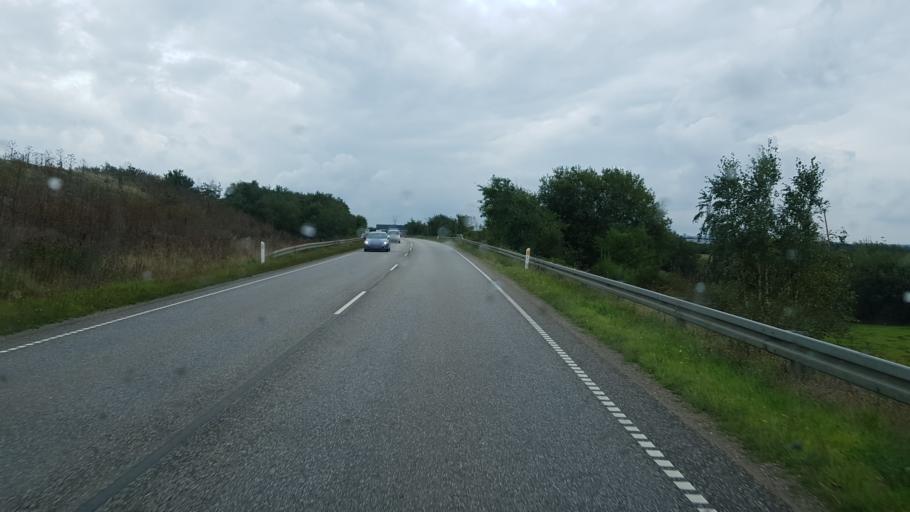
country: DK
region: Central Jutland
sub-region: Horsens Kommune
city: Horsens
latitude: 55.8920
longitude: 9.7615
